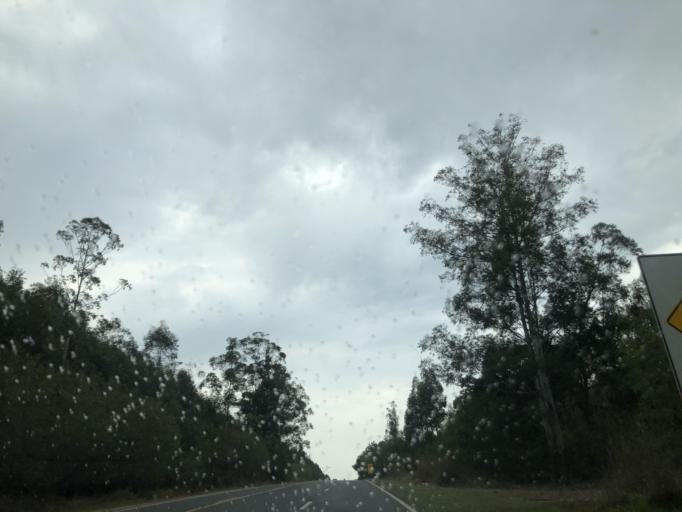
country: BR
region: Sao Paulo
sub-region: Salto De Pirapora
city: Salto de Pirapora
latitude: -23.6743
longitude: -47.6025
